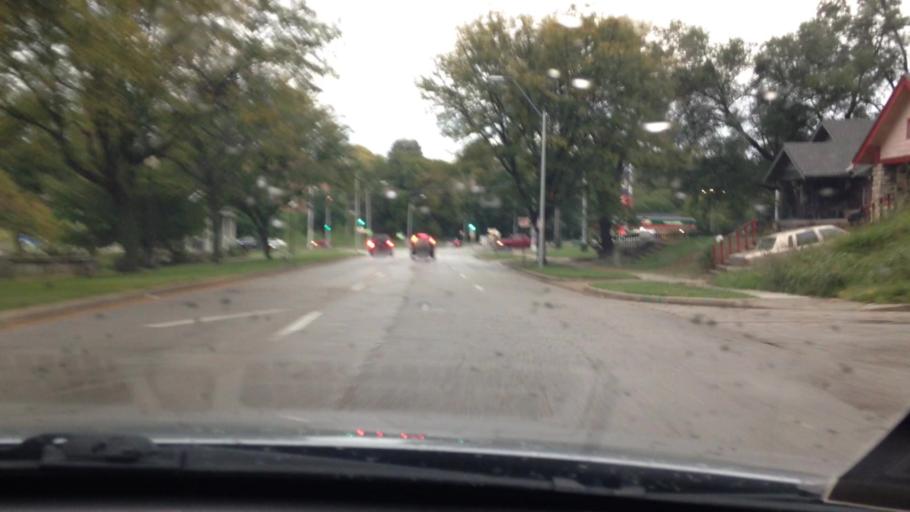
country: US
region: Kansas
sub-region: Johnson County
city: Mission Hills
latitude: 39.0141
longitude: -94.5704
